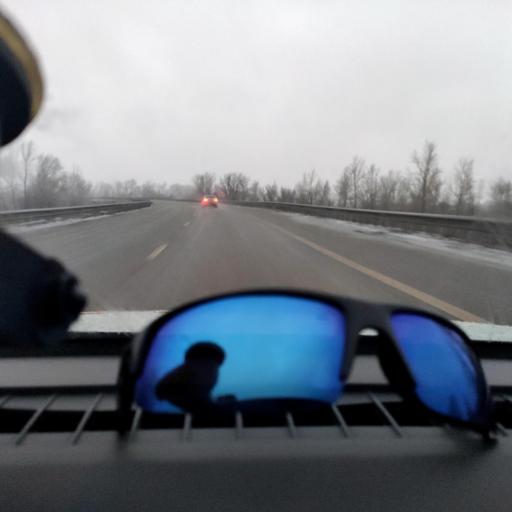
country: RU
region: Samara
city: Novosemeykino
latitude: 53.4143
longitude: 50.3400
